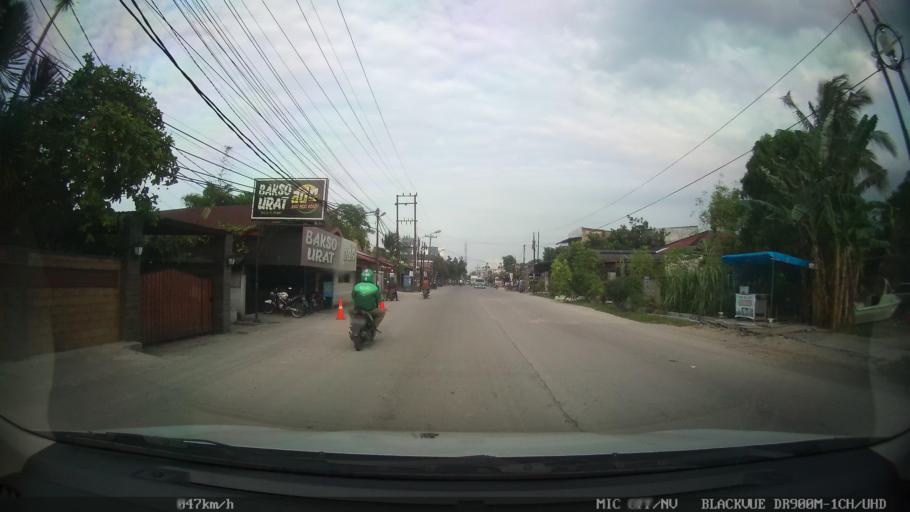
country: ID
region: North Sumatra
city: Sunggal
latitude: 3.5634
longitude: 98.6228
